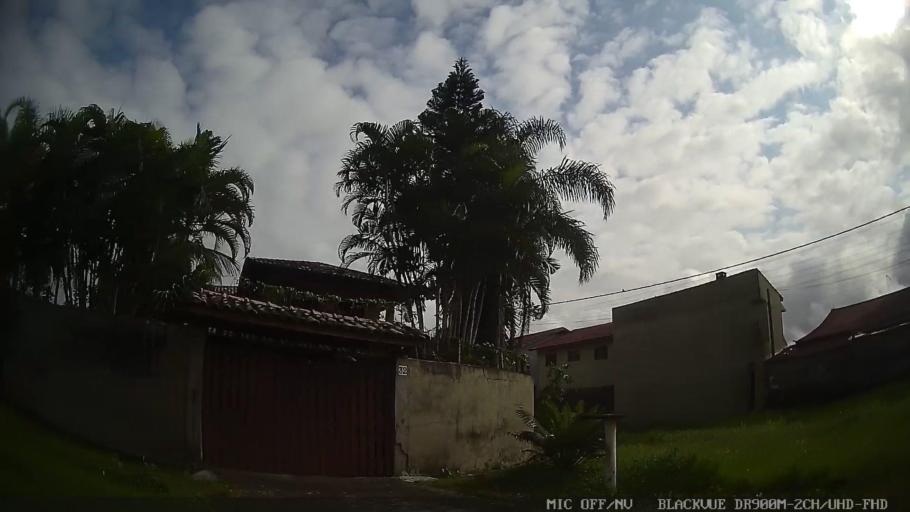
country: BR
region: Sao Paulo
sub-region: Itanhaem
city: Itanhaem
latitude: -24.2000
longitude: -46.8274
